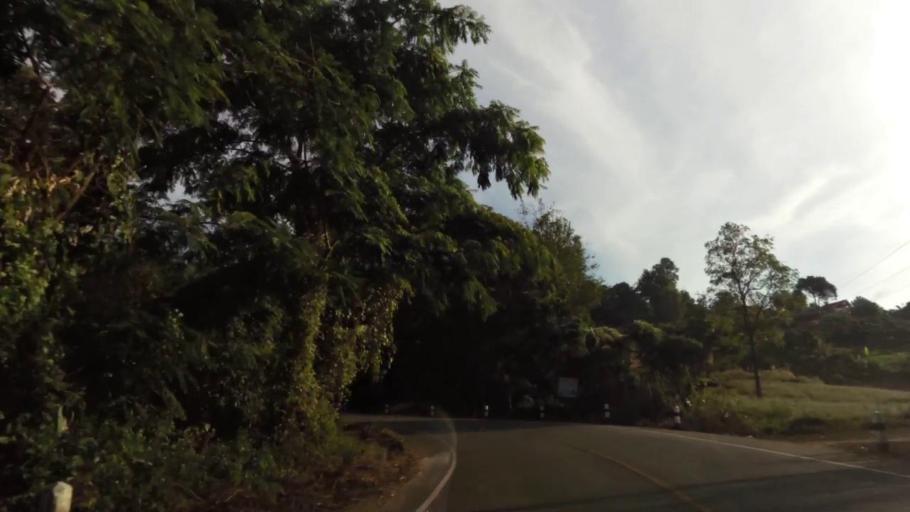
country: TH
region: Chiang Rai
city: Khun Tan
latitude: 19.8622
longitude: 100.4301
